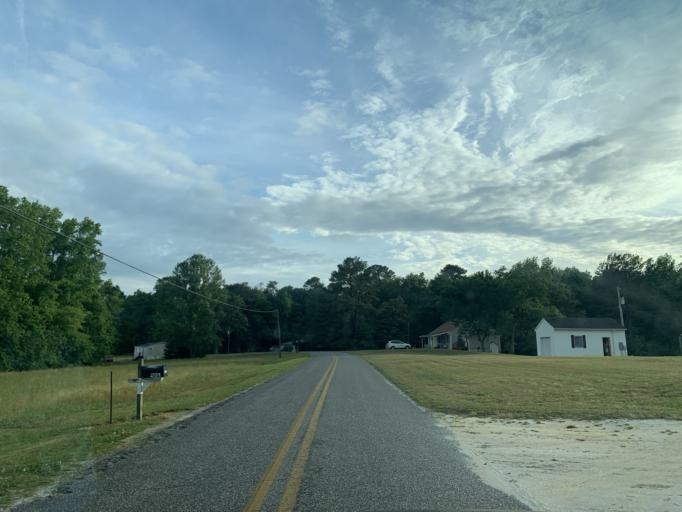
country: US
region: Maryland
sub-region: Worcester County
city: Pocomoke City
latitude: 38.0802
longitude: -75.4767
